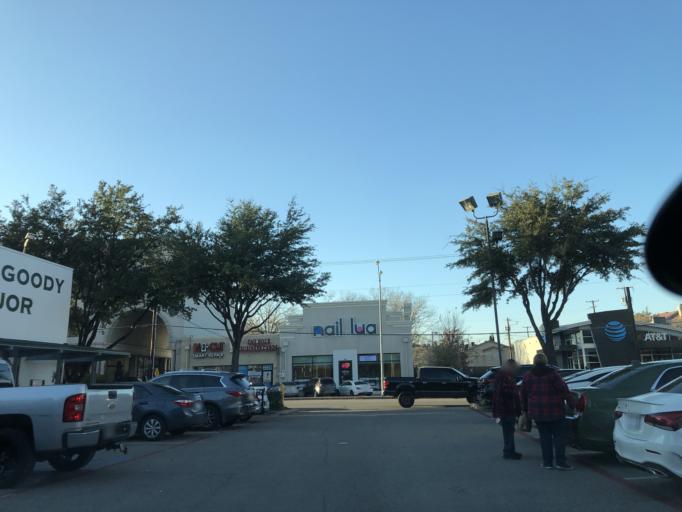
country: US
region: Texas
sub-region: Dallas County
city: Highland Park
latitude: 32.8105
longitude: -96.8068
